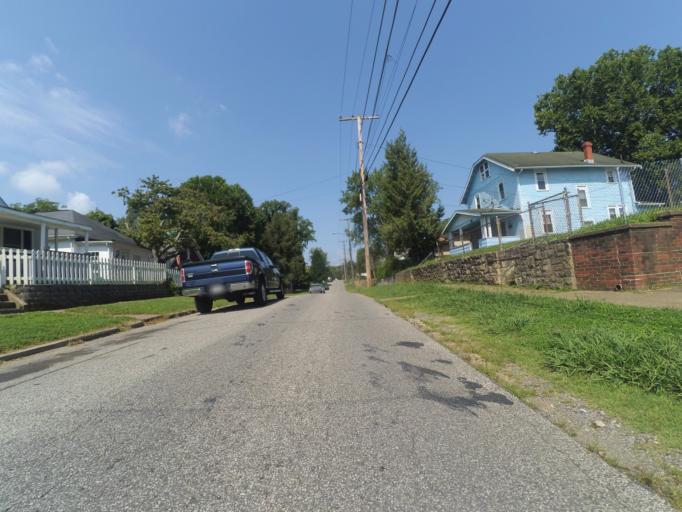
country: US
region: West Virginia
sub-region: Cabell County
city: Huntington
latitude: 38.4113
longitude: -82.4063
